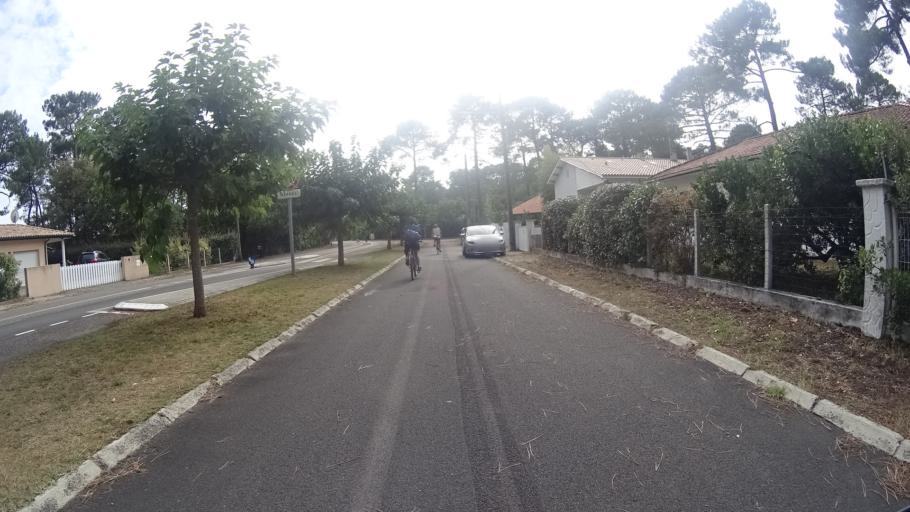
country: FR
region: Aquitaine
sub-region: Departement de la Gironde
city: Lacanau
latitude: 44.9950
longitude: -1.1450
